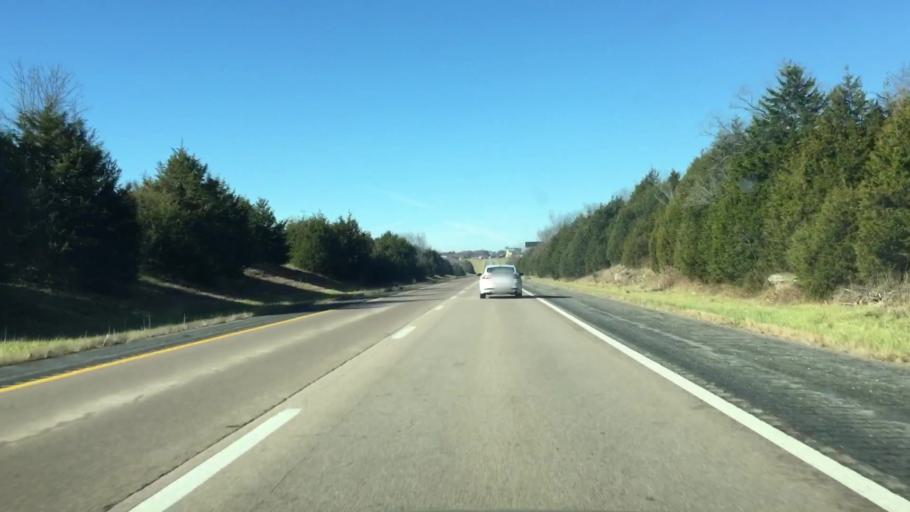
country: US
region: Missouri
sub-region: Miller County
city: Eldon
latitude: 38.3677
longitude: -92.4878
